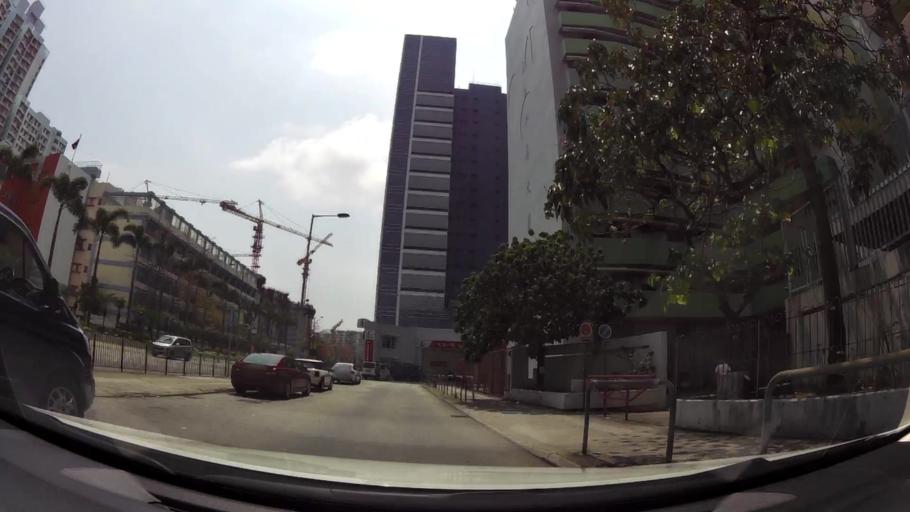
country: HK
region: Sham Shui Po
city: Sham Shui Po
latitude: 22.3345
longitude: 114.1526
